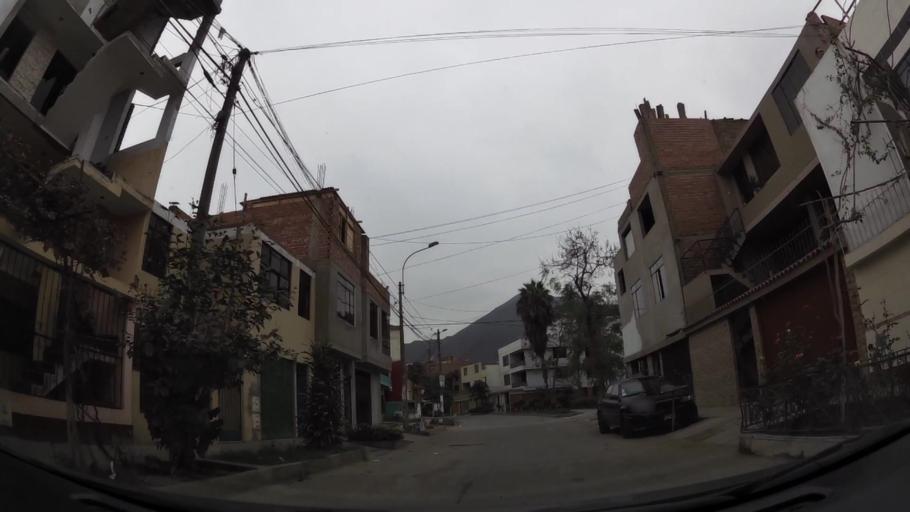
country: PE
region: Lima
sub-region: Lima
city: Independencia
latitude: -11.9681
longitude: -77.0590
